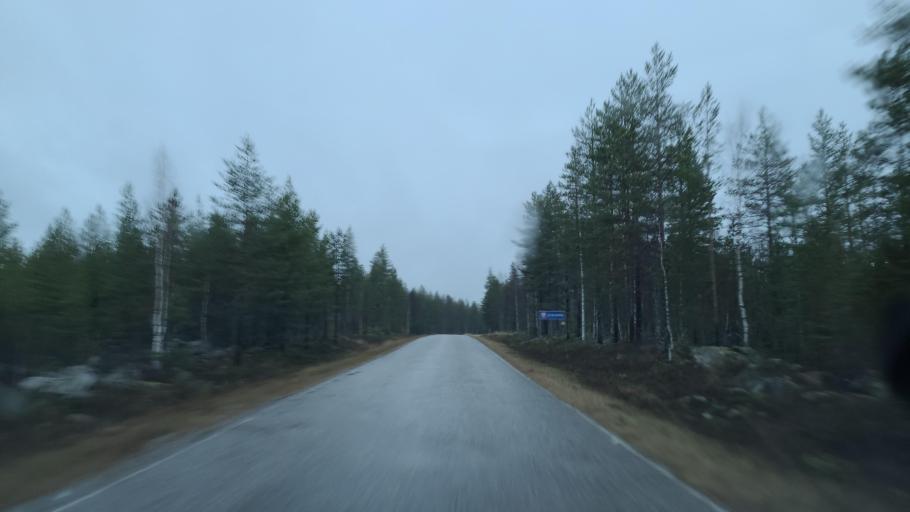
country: FI
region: Lapland
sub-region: Kemi-Tornio
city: Simo
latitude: 65.9167
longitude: 25.2003
